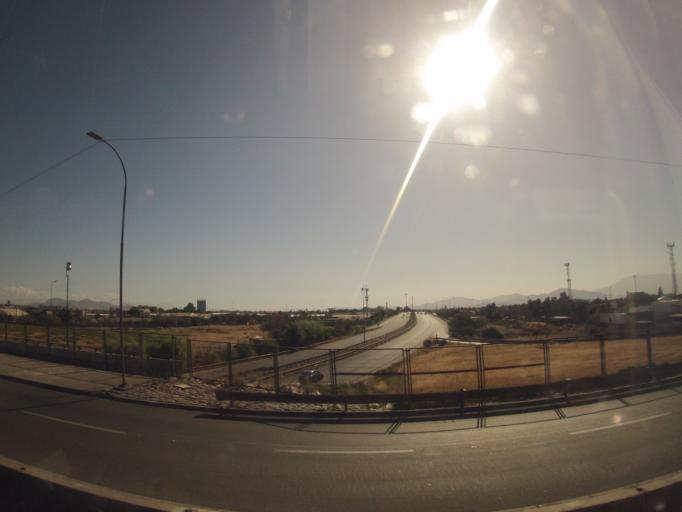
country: CL
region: Santiago Metropolitan
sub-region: Provincia de Santiago
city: Santiago
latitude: -33.4766
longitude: -70.6862
